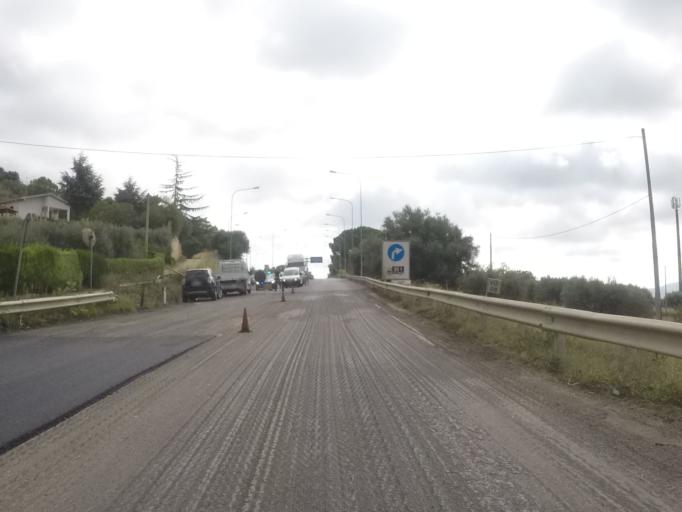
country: IT
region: Sicily
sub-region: Provincia di Caltanissetta
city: Caltanissetta
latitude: 37.4733
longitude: 14.0242
